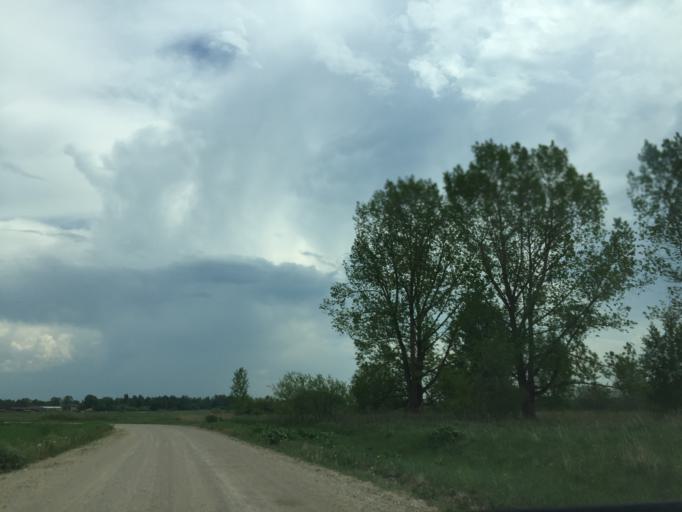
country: LV
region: Livani
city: Livani
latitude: 56.5501
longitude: 26.2296
